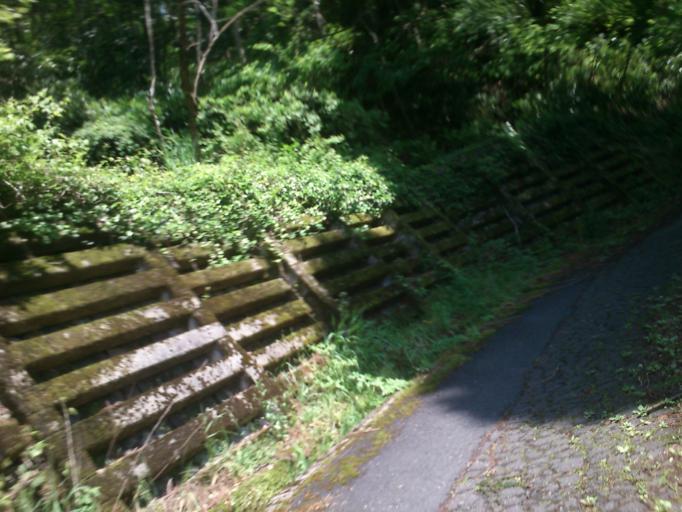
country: JP
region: Kyoto
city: Miyazu
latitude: 35.7119
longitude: 135.1618
